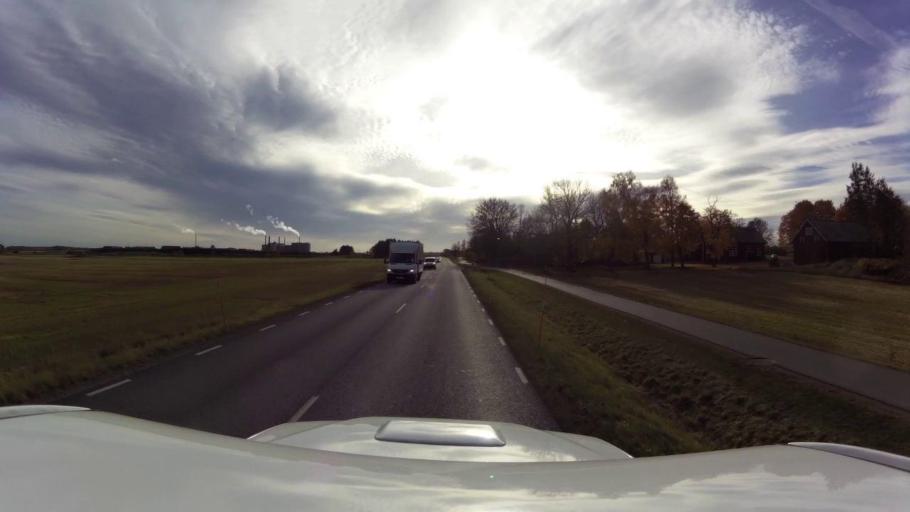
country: SE
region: OEstergoetland
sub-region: Linkopings Kommun
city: Ekangen
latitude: 58.4469
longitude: 15.6455
